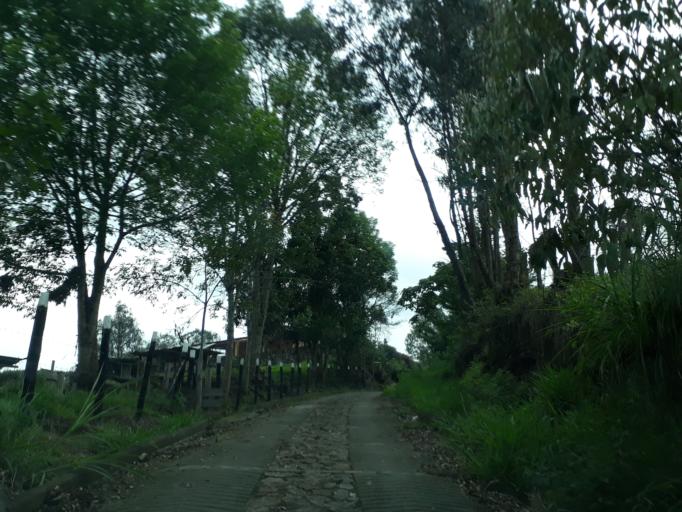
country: CO
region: Cundinamarca
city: Manta
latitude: 5.0021
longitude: -73.5357
